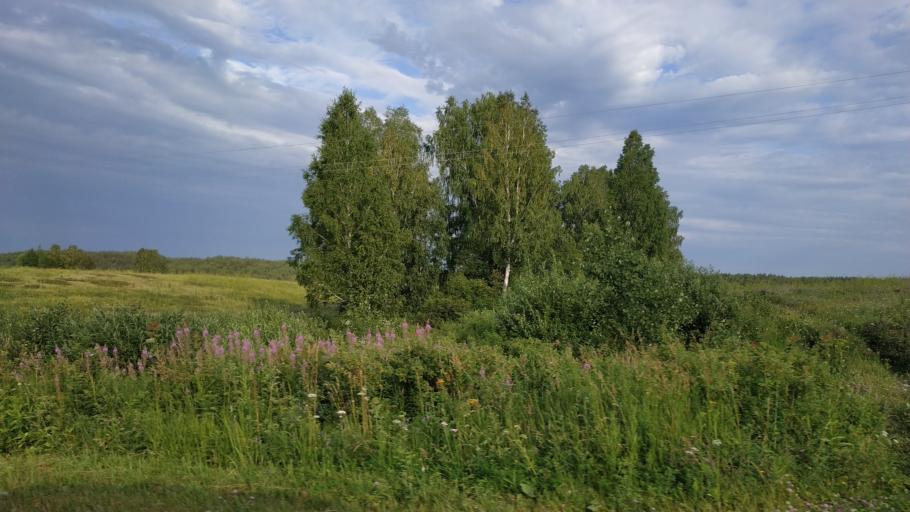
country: RU
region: Sverdlovsk
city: Yelanskiy
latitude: 57.0689
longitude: 62.4334
